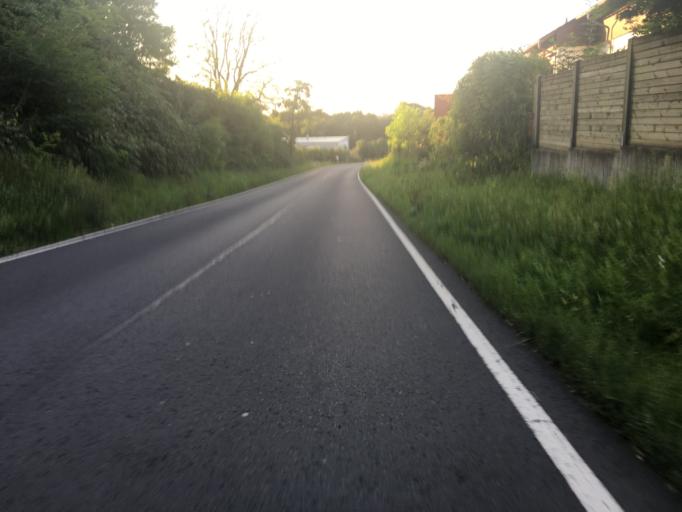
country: DE
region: Hesse
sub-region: Regierungsbezirk Darmstadt
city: Gelnhausen
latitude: 50.1859
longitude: 9.1476
